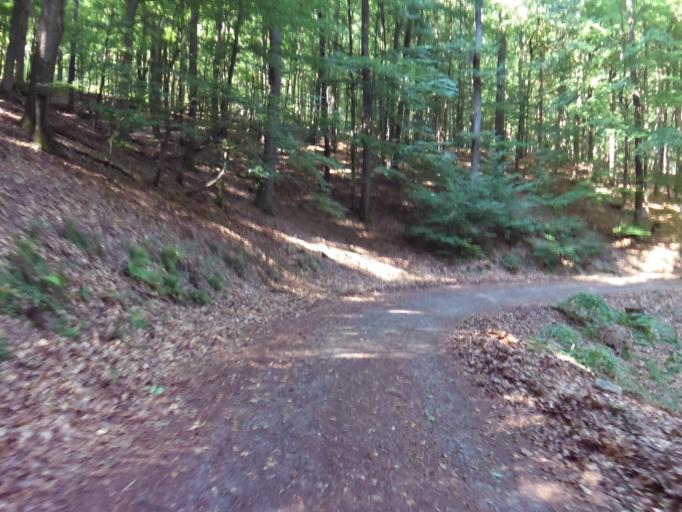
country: DE
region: Rheinland-Pfalz
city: Neidenfels
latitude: 49.4180
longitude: 8.0570
